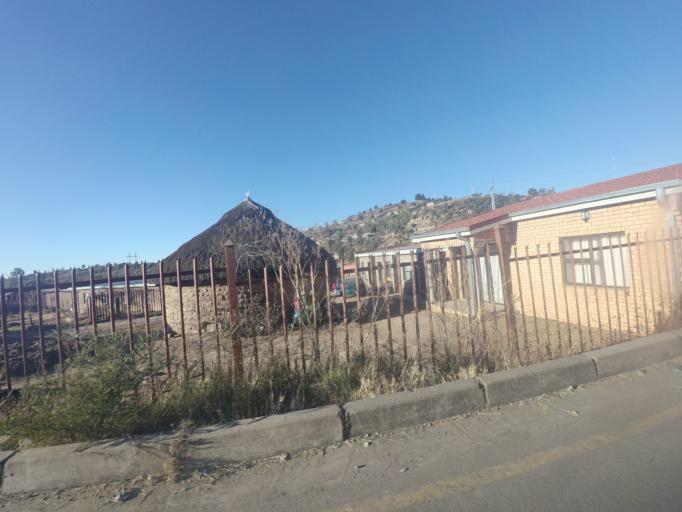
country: LS
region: Maseru
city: Maseru
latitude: -29.3267
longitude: 27.5169
